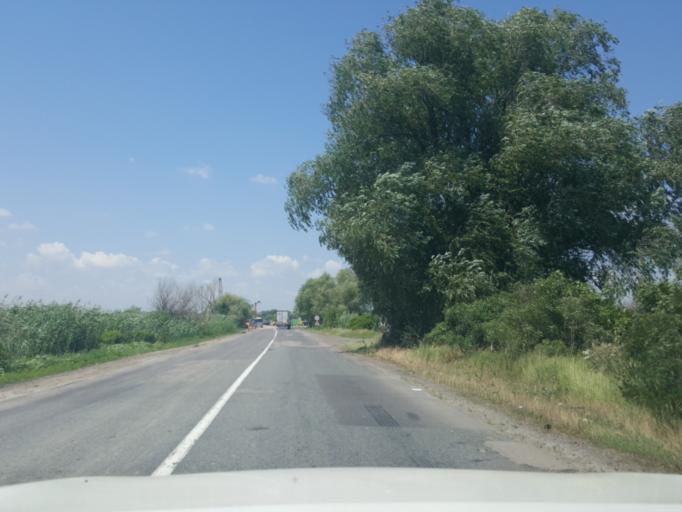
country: UA
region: Odessa
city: Bilyayivka
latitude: 46.4136
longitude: 30.1604
